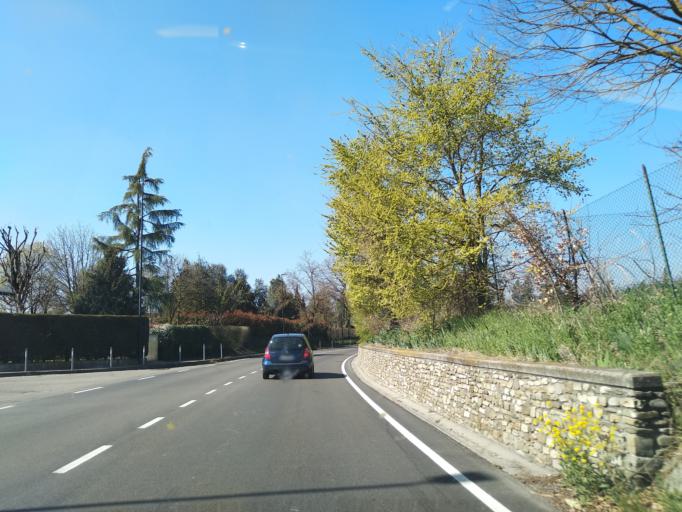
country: IT
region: Emilia-Romagna
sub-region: Provincia di Reggio Emilia
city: Albinea
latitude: 44.6230
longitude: 10.5955
